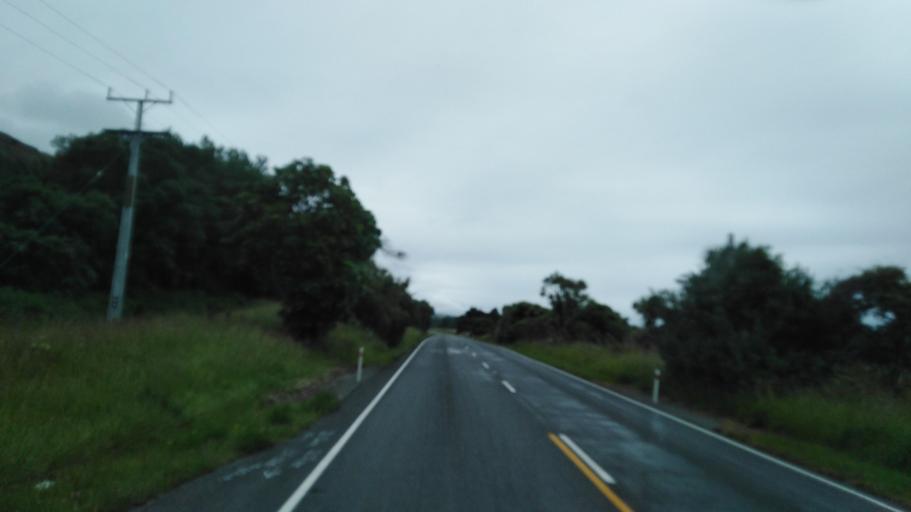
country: NZ
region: Canterbury
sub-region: Kaikoura District
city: Kaikoura
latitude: -42.0789
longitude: 173.9405
